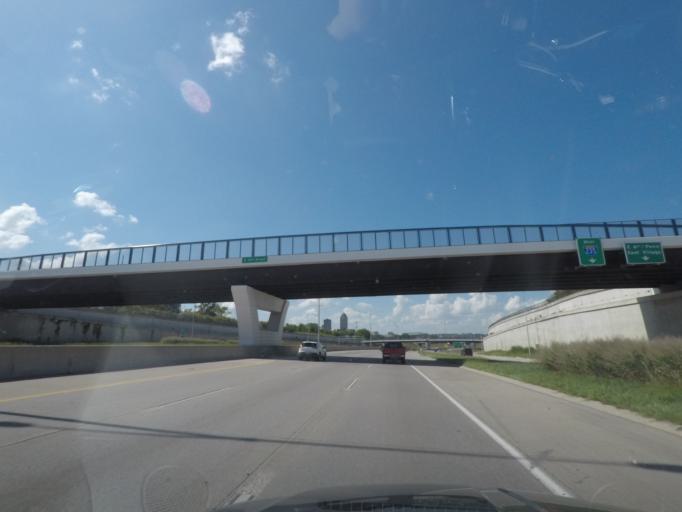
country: US
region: Iowa
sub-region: Polk County
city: Des Moines
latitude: 41.5955
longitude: -93.6026
